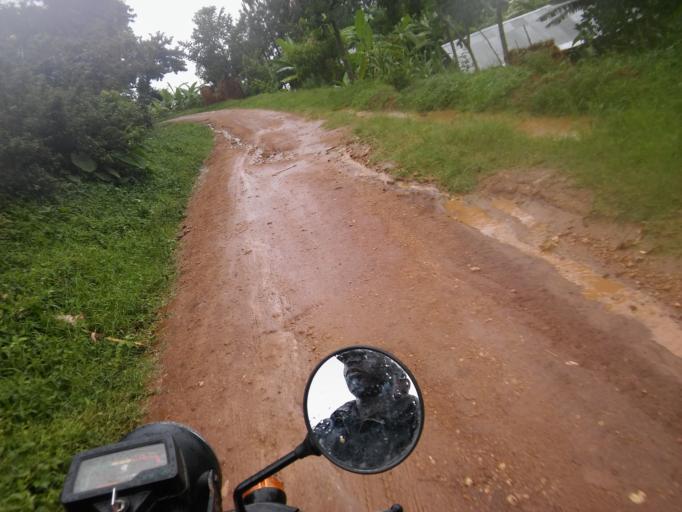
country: UG
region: Eastern Region
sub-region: Bududa District
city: Bududa
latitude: 0.9999
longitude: 34.2434
